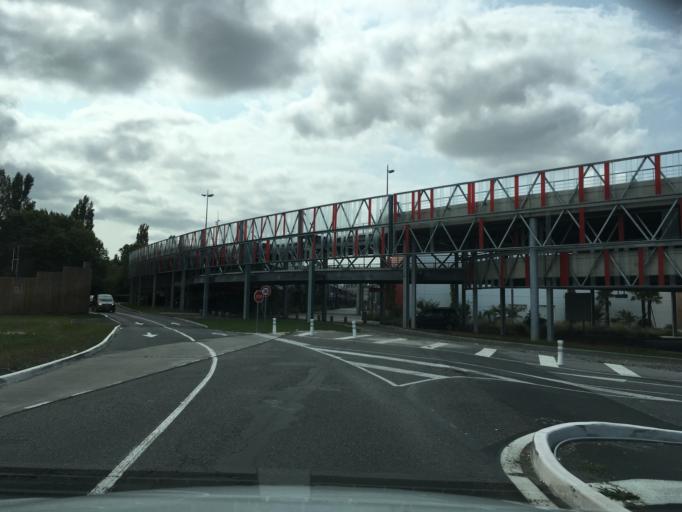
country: FR
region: Aquitaine
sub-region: Departement des Pyrenees-Atlantiques
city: Bayonne
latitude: 43.4897
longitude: -1.4961
